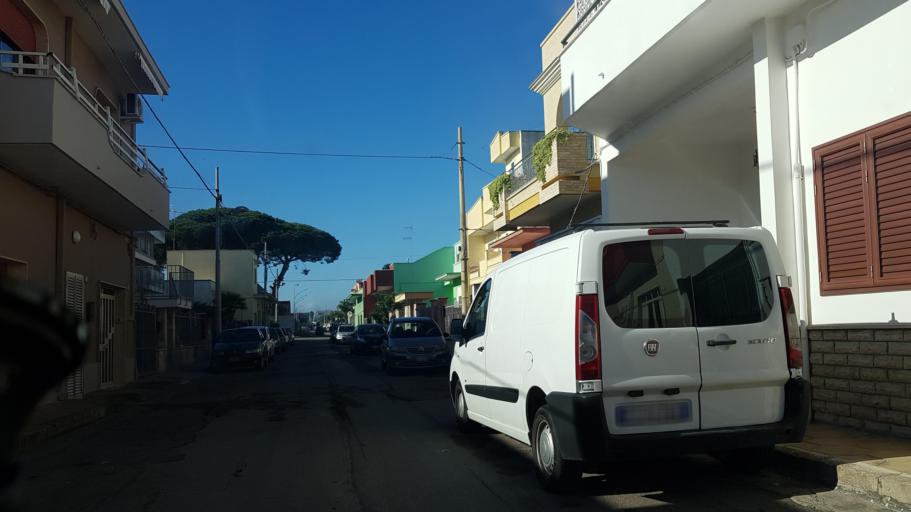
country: IT
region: Apulia
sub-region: Provincia di Lecce
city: Squinzano
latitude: 40.4281
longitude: 18.0453
